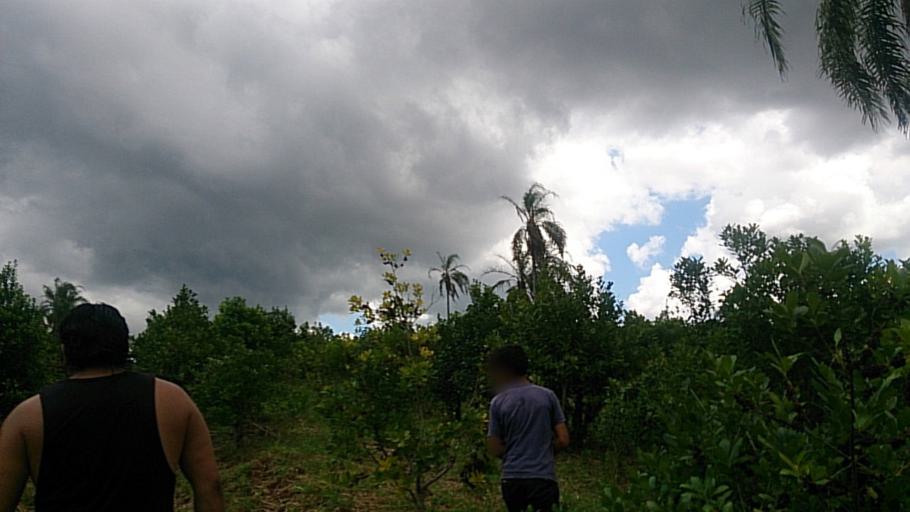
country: AR
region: Misiones
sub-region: Departamento de Obera
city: Obera
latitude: -27.5117
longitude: -55.1073
